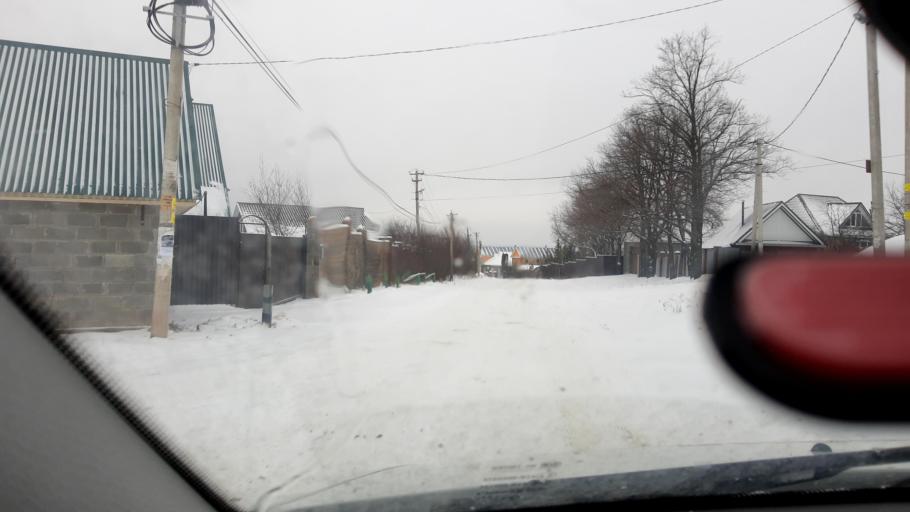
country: RU
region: Bashkortostan
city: Kabakovo
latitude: 54.6323
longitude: 56.0822
